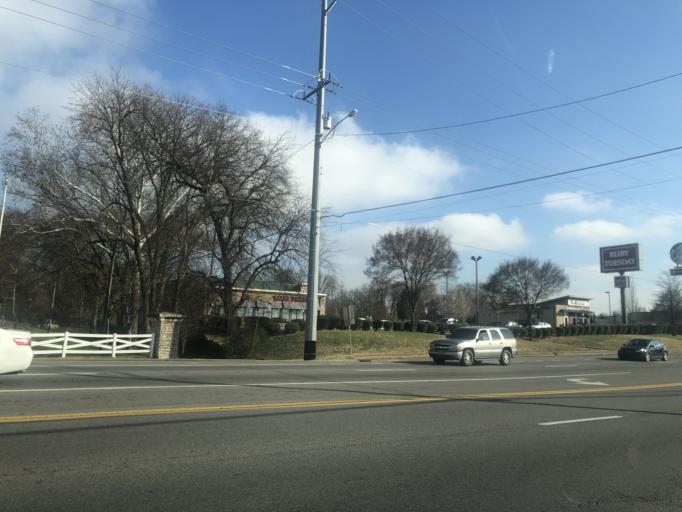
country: US
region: Tennessee
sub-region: Rutherford County
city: La Vergne
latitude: 36.0866
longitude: -86.6487
